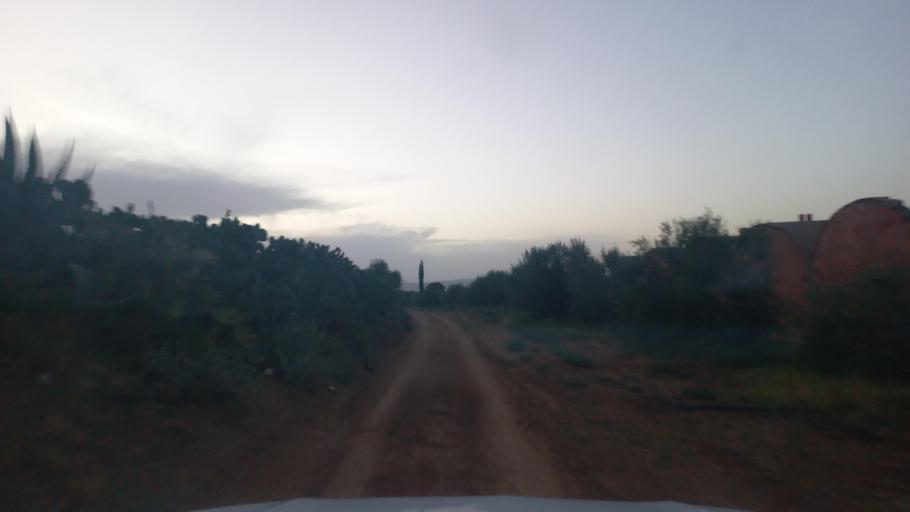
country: TN
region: Al Qasrayn
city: Kasserine
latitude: 35.2310
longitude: 9.0347
